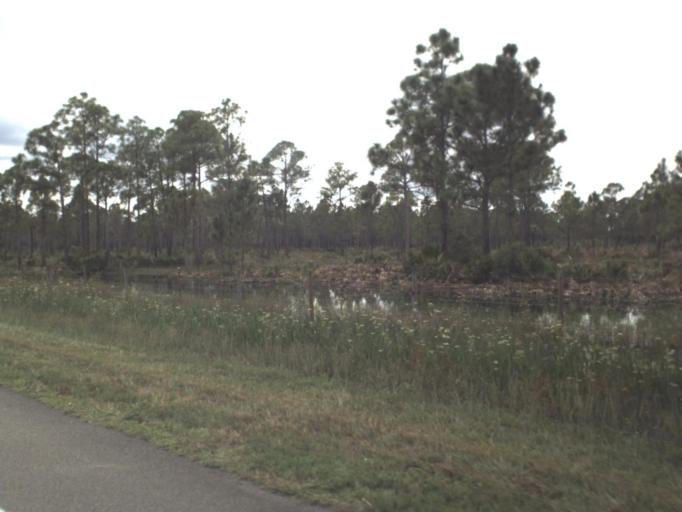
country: US
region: Florida
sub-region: Lee County
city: Olga
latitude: 26.9144
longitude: -81.7604
